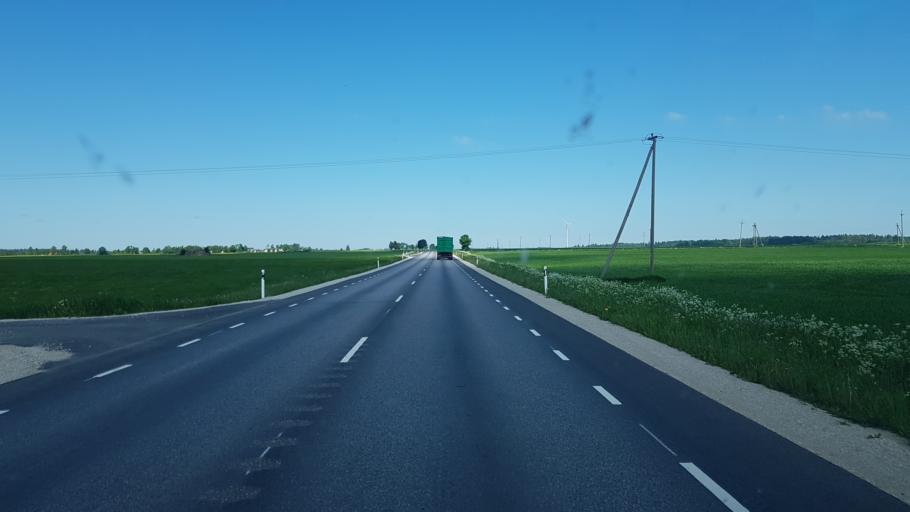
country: EE
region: Laeaene-Virumaa
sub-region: Vaeike-Maarja vald
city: Vaike-Maarja
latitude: 59.1659
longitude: 26.2670
